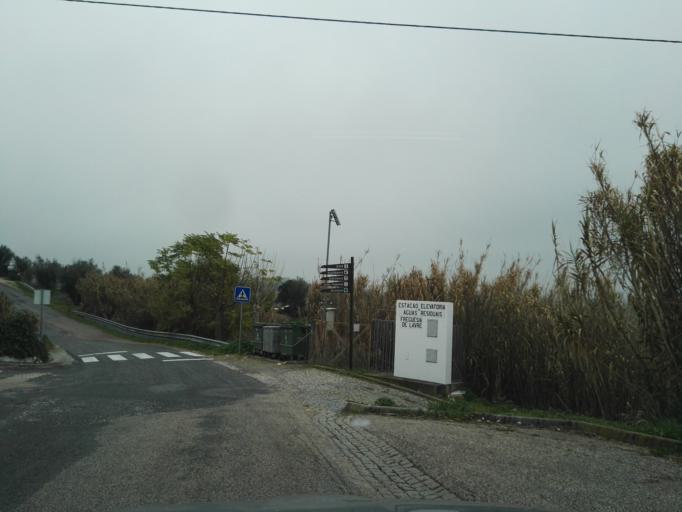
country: PT
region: Evora
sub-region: Vendas Novas
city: Vendas Novas
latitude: 38.7748
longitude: -8.3668
